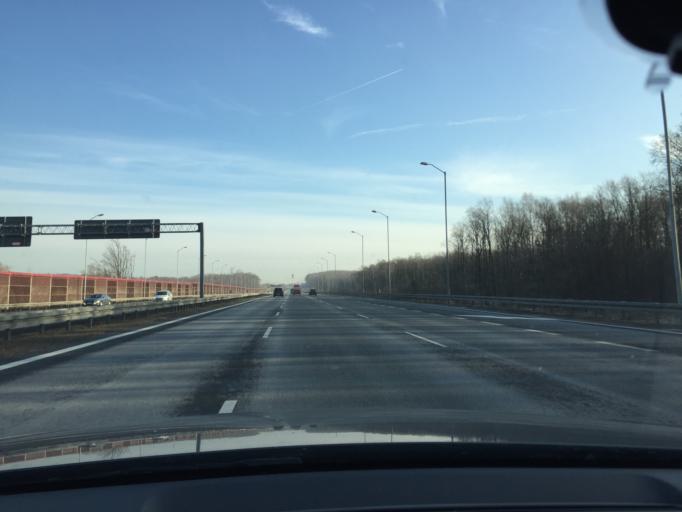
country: PL
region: Silesian Voivodeship
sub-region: Ruda Slaska
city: Ruda Slaska
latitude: 50.2548
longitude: 18.8623
